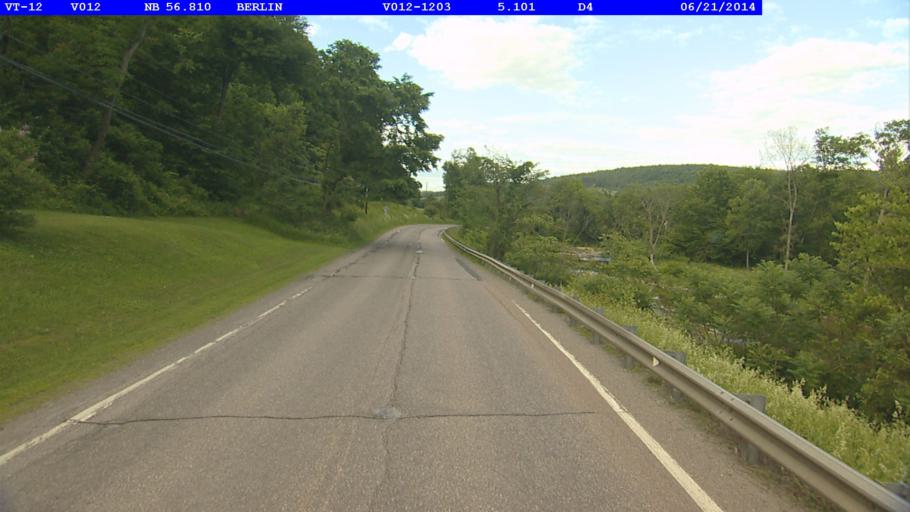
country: US
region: Vermont
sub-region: Washington County
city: Montpelier
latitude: 44.2287
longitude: -72.6049
